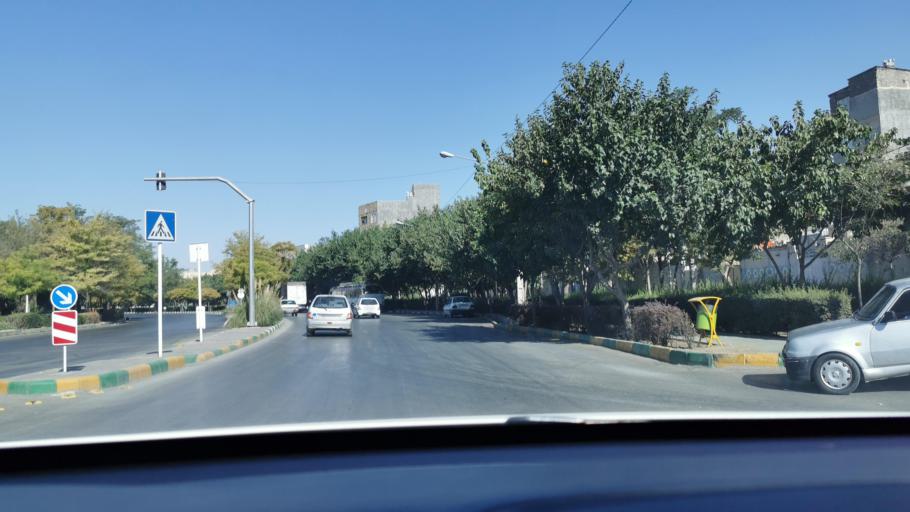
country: IR
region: Razavi Khorasan
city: Mashhad
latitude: 36.3349
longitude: 59.6346
